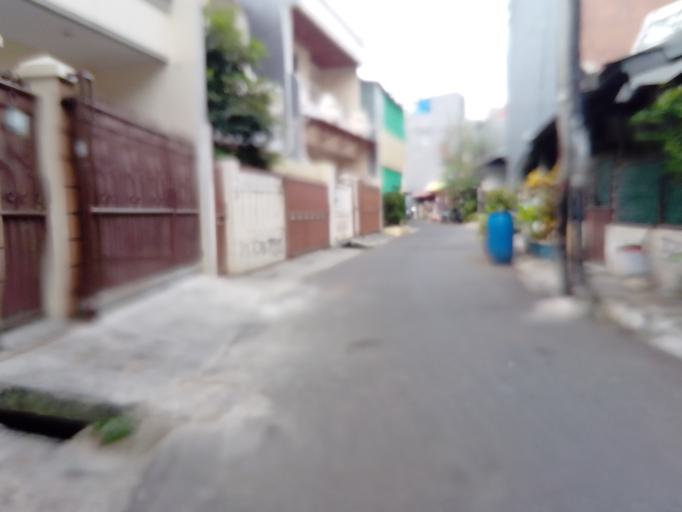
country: ID
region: Jakarta Raya
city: Jakarta
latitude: -6.1535
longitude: 106.8145
